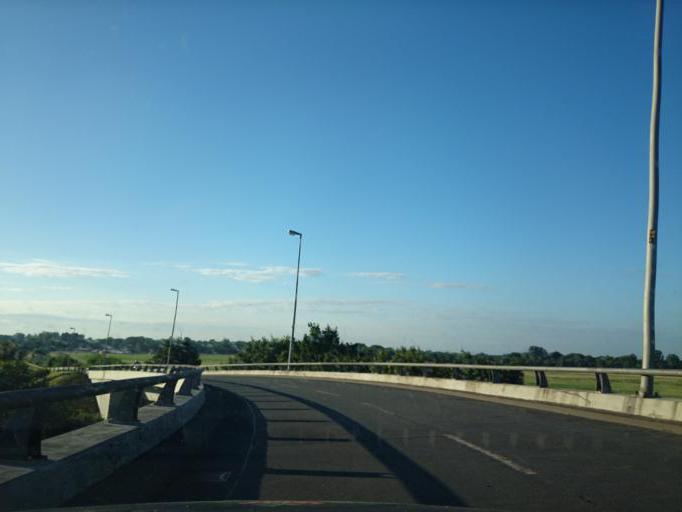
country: DE
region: Berlin
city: Tegel
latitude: 52.5651
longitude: 13.3105
